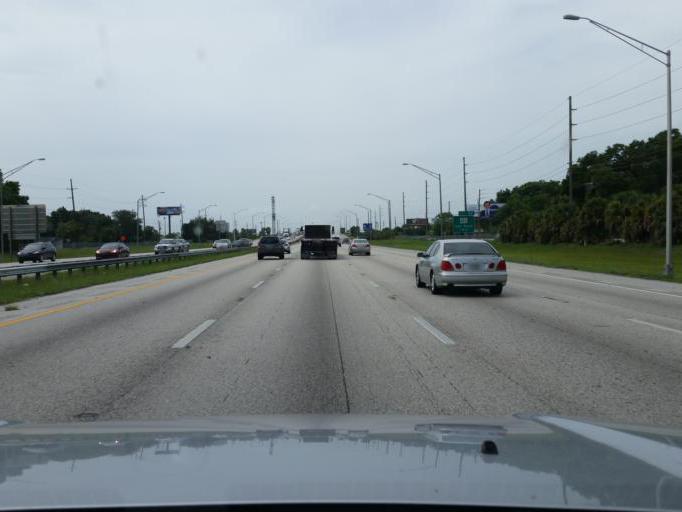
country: US
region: Florida
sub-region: Orange County
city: Eatonville
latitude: 28.6233
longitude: -81.3867
